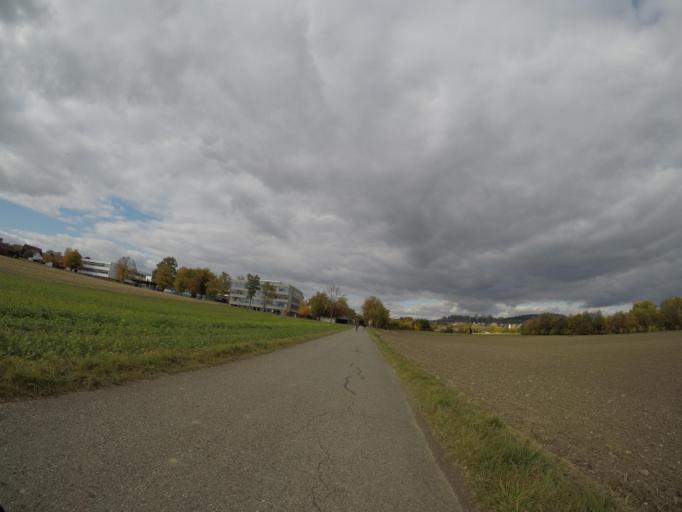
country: DE
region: Baden-Wuerttemberg
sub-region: Tuebingen Region
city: Munderkingen
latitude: 48.2287
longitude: 9.6500
